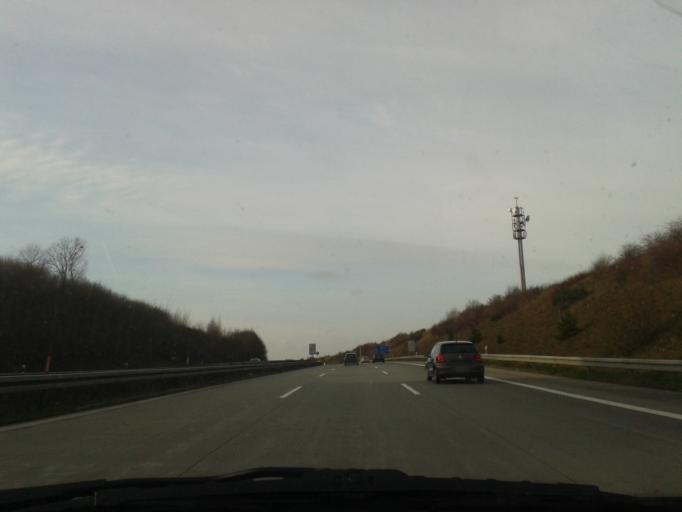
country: DE
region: Saxony
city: Freital
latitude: 51.0357
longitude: 13.6331
